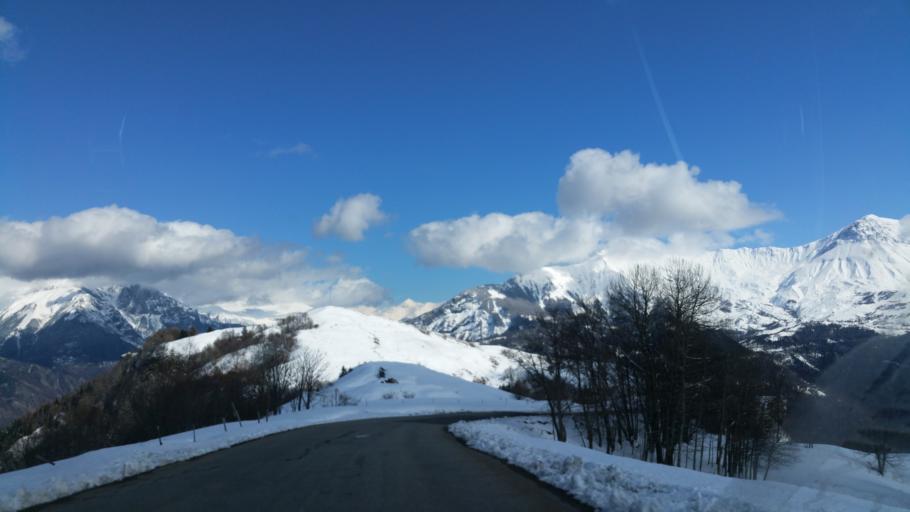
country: FR
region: Rhone-Alpes
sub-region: Departement de la Savoie
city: Saint-Jean-de-Maurienne
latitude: 45.2601
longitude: 6.2867
